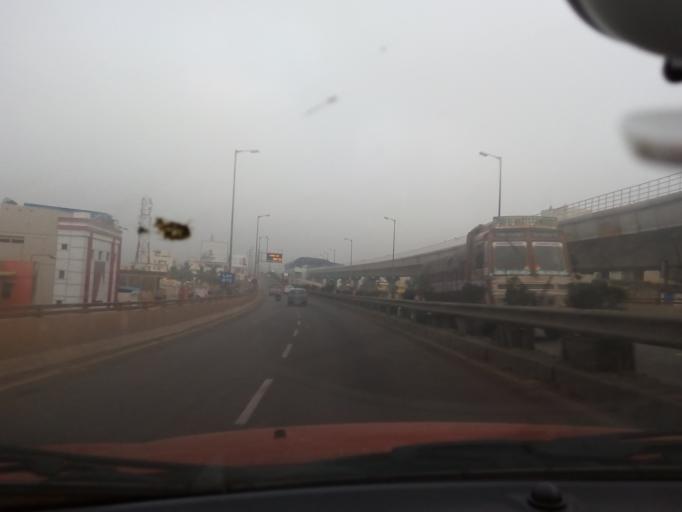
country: IN
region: Karnataka
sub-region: Bangalore Urban
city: Yelahanka
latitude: 13.0417
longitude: 77.5161
